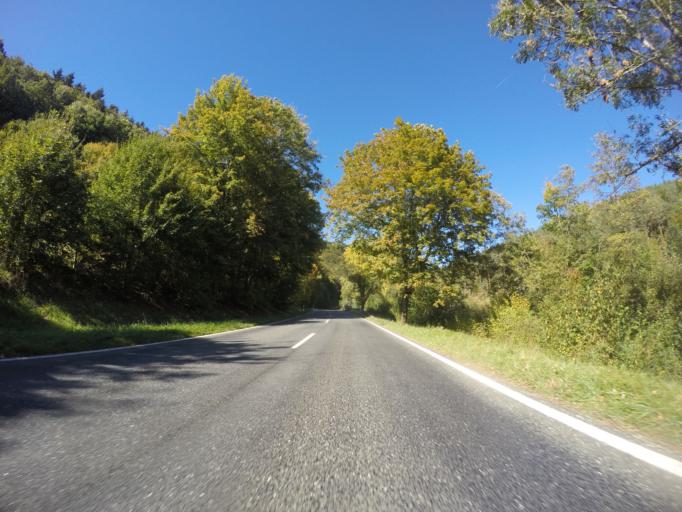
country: DE
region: Bavaria
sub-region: Upper Franconia
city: Gossweinstein
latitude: 49.7828
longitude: 11.3330
